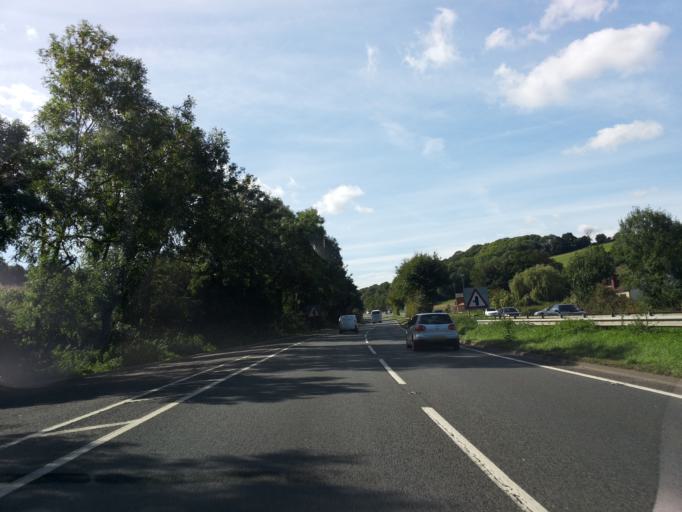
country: GB
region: England
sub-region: Kent
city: Newington
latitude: 51.3181
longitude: 0.6443
